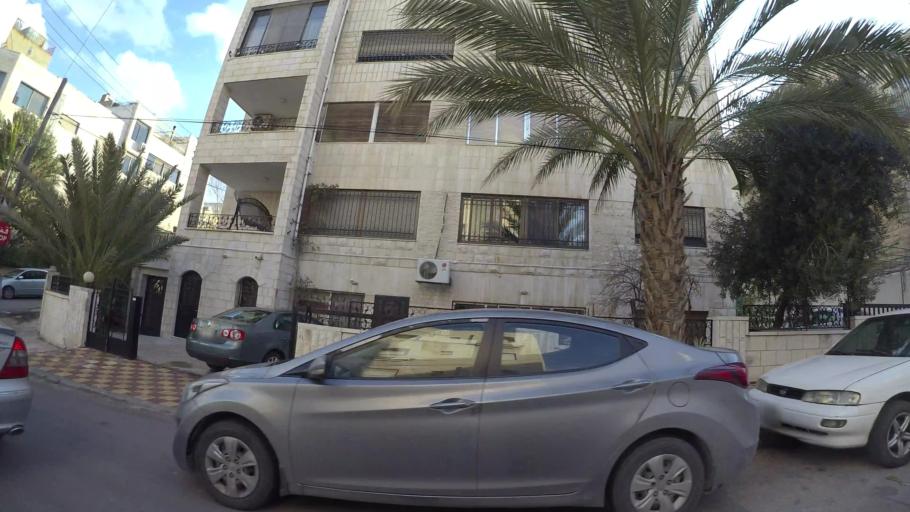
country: JO
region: Amman
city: Al Jubayhah
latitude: 31.9802
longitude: 35.8900
